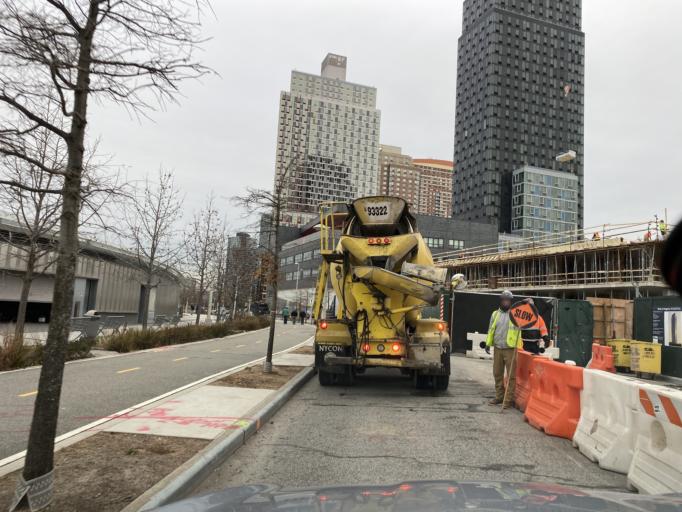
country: US
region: New York
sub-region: Queens County
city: Long Island City
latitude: 40.7417
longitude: -73.9605
